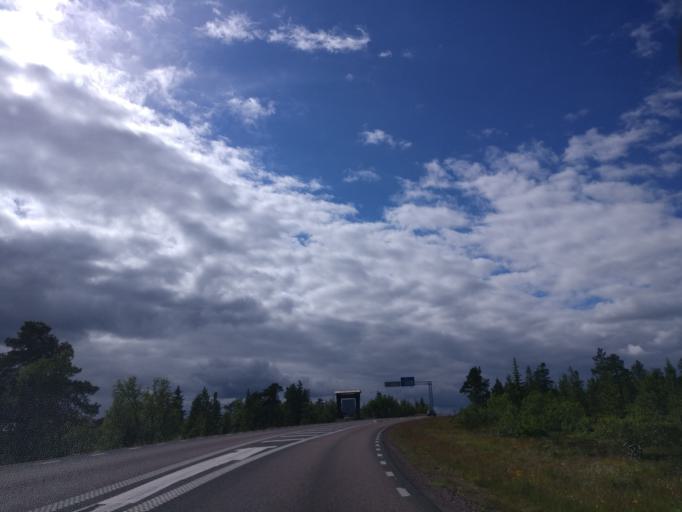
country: SE
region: Dalarna
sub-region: Malung-Saelens kommun
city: Malung
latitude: 61.1566
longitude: 13.1260
